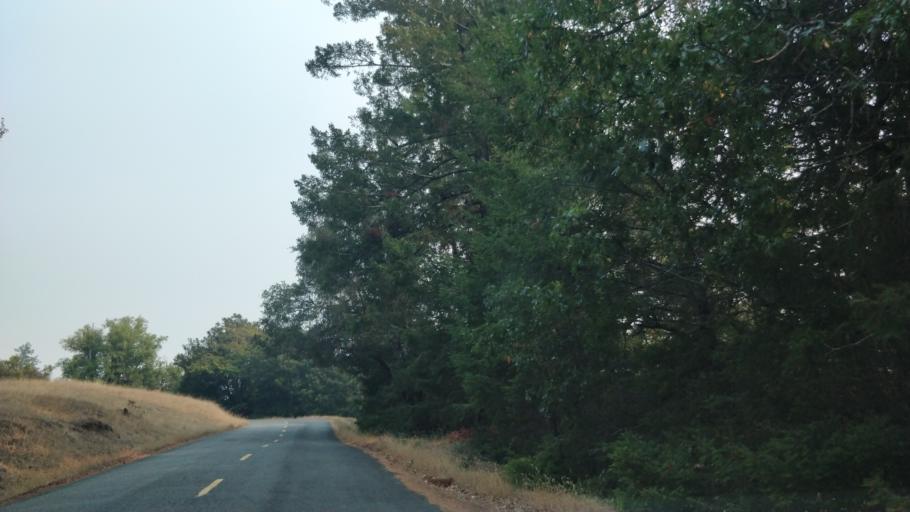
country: US
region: California
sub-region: Humboldt County
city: Rio Dell
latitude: 40.2476
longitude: -124.1220
